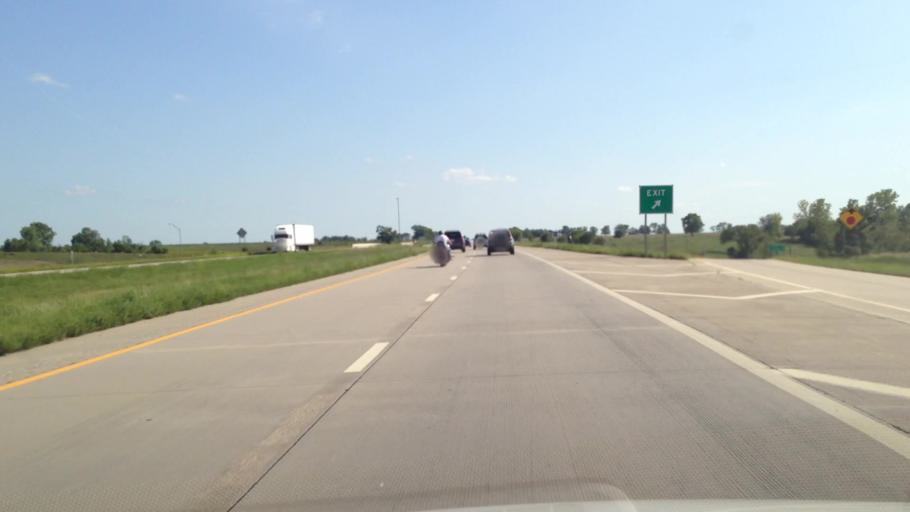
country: US
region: Kansas
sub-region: Bourbon County
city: Fort Scott
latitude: 37.9962
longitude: -94.7051
